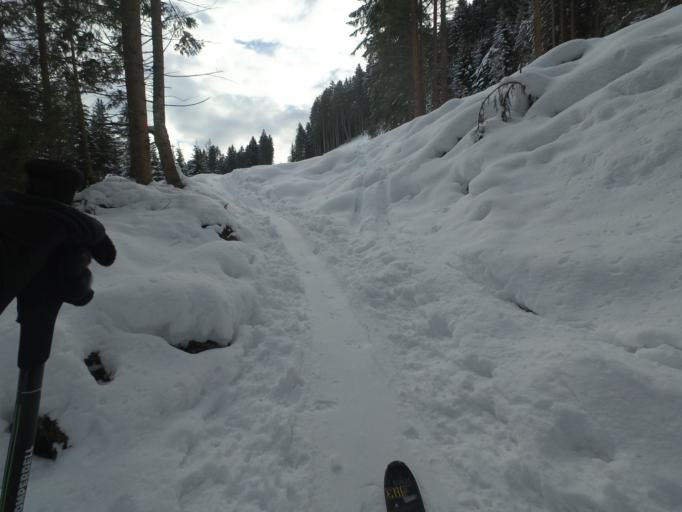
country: AT
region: Salzburg
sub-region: Politischer Bezirk Sankt Johann im Pongau
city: Sankt Johann im Pongau
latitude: 47.3239
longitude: 13.2160
